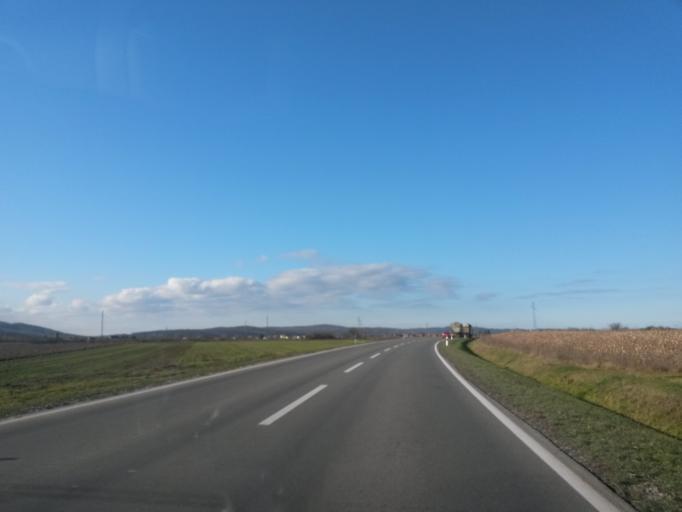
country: HR
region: Virovitick-Podravska
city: Slatina
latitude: 45.7165
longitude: 17.6826
